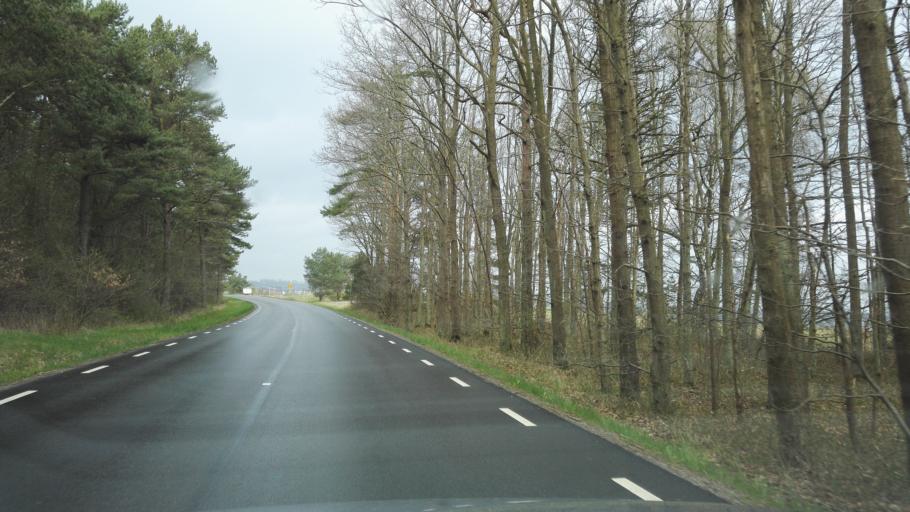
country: SE
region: Skane
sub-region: Simrishamns Kommun
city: Simrishamn
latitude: 55.4648
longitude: 14.2782
